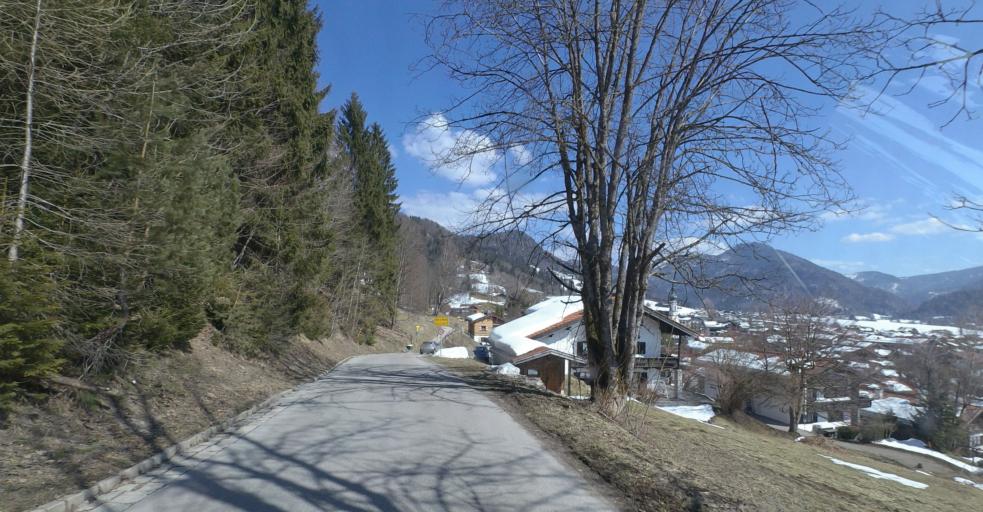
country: DE
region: Bavaria
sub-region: Upper Bavaria
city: Reit im Winkl
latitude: 47.6784
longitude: 12.4645
